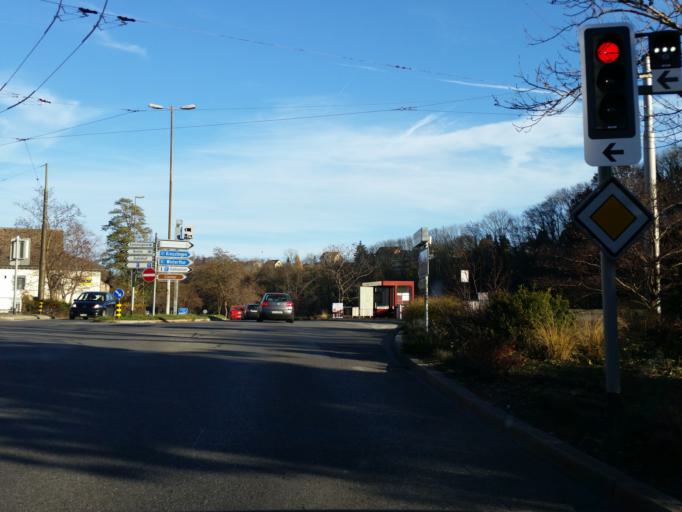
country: CH
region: Schaffhausen
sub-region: Bezirk Schaffhausen
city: Schaffhausen
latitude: 47.6936
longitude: 8.6313
